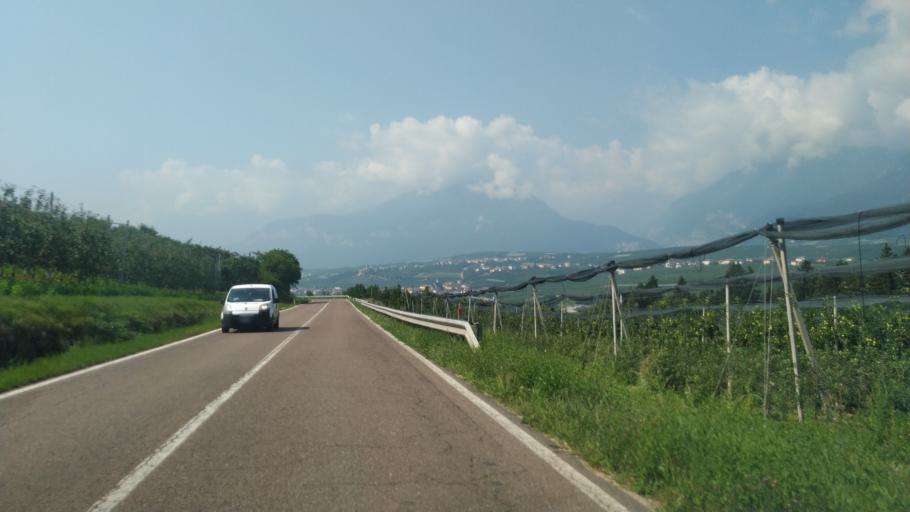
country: IT
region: Trentino-Alto Adige
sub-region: Provincia di Trento
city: Sanzeno
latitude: 46.3520
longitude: 11.0669
